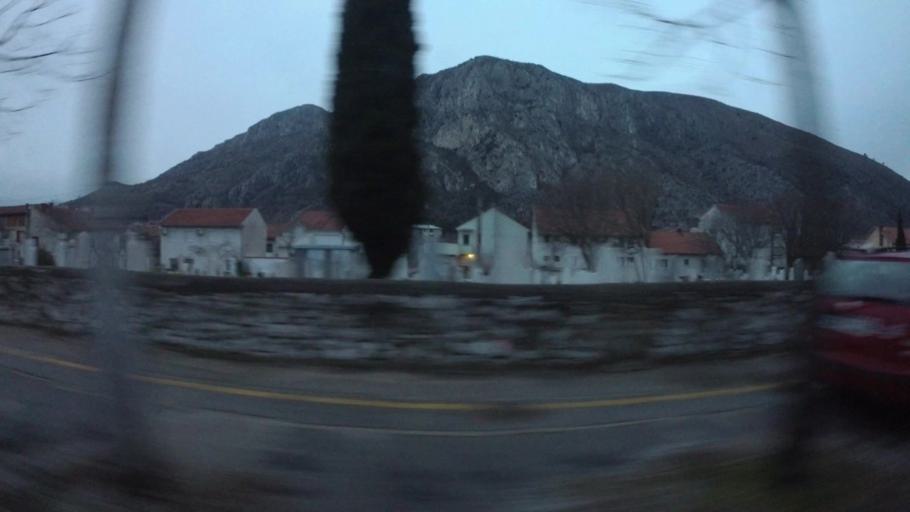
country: BA
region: Federation of Bosnia and Herzegovina
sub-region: Hercegovacko-Bosanski Kanton
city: Mostar
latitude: 43.3301
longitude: 17.8193
